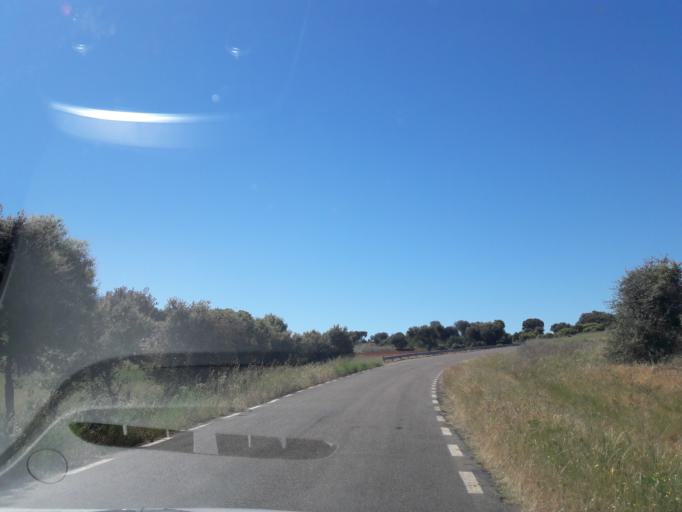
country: ES
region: Castille and Leon
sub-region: Provincia de Salamanca
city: Parada de Arriba
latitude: 41.0035
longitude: -5.8125
